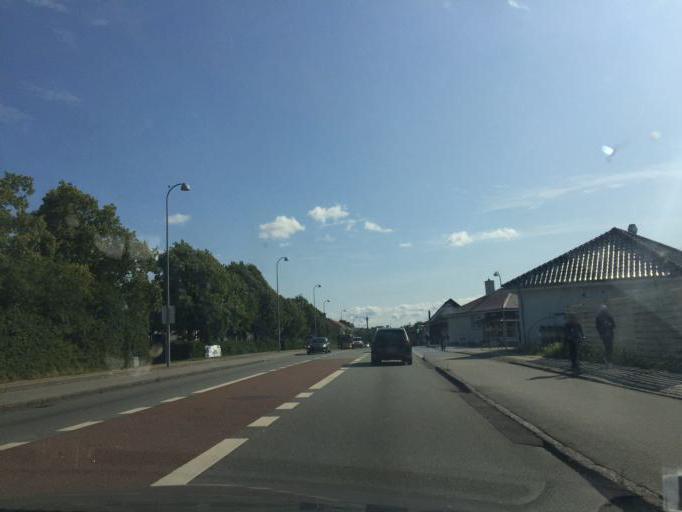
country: DK
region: Capital Region
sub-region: Herlev Kommune
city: Herlev
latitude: 55.7232
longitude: 12.4718
